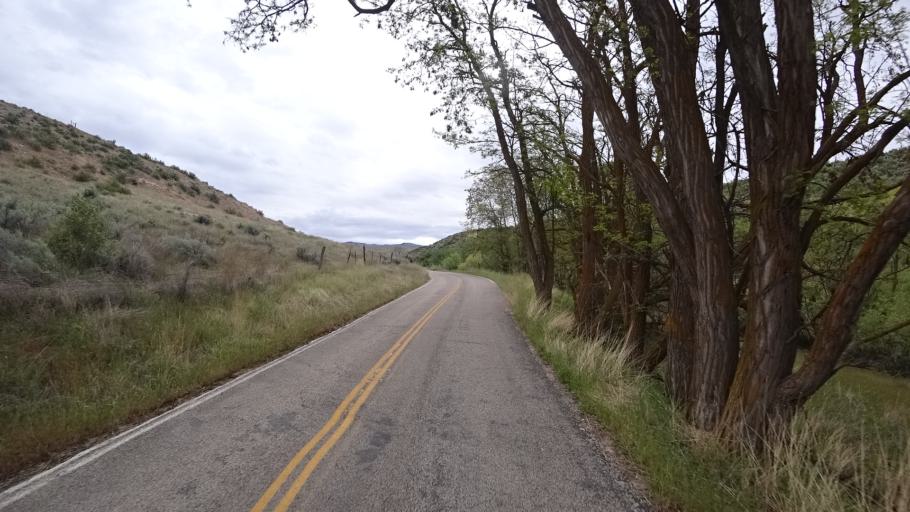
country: US
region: Idaho
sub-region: Ada County
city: Boise
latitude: 43.6163
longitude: -116.1575
